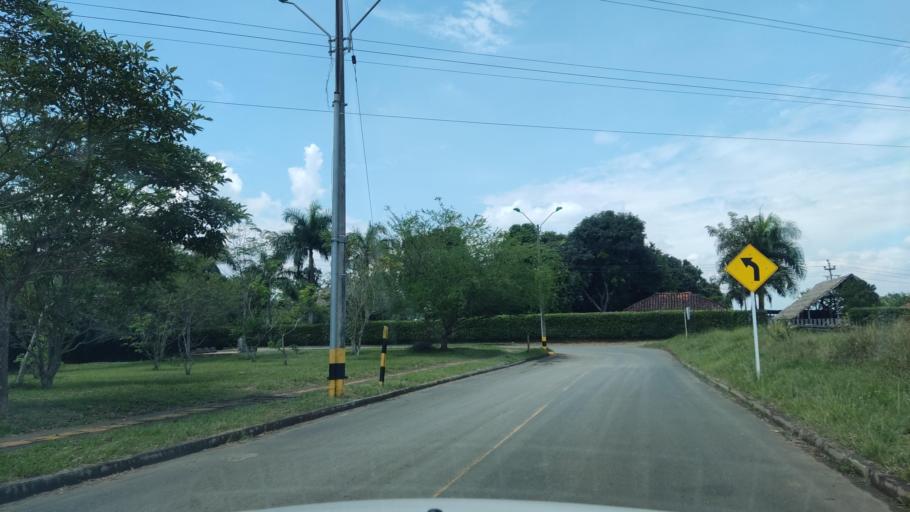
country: CO
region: Valle del Cauca
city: Jamundi
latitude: 3.3015
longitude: -76.5544
